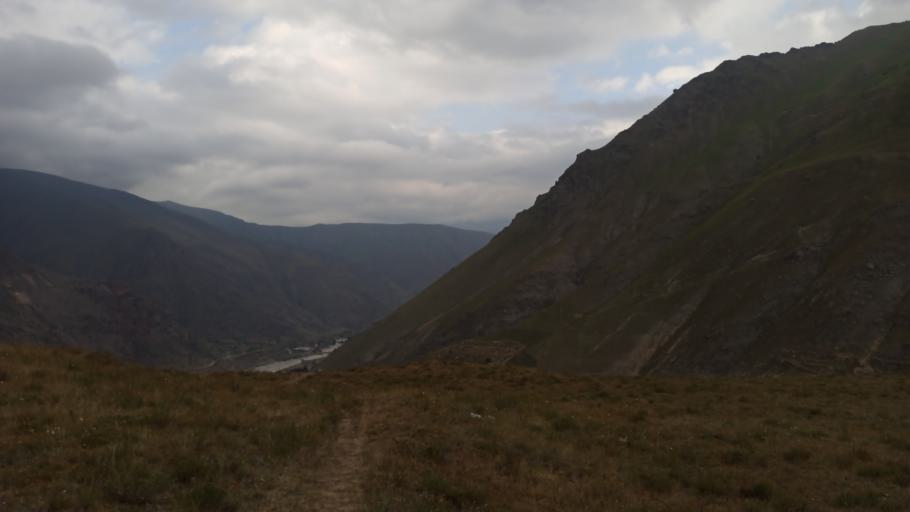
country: RU
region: Kabardino-Balkariya
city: Tyrnyauz
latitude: 43.3912
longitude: 42.9267
